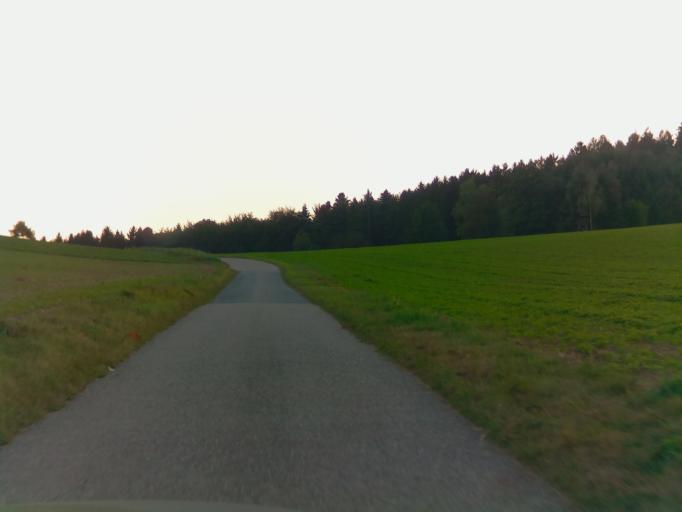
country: DE
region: Hesse
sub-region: Regierungsbezirk Darmstadt
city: Wald-Michelbach
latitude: 49.5951
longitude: 8.8336
